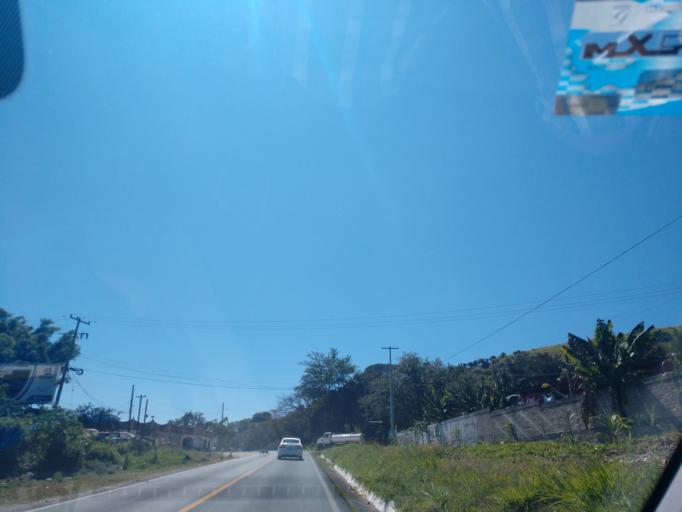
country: MX
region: Nayarit
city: Xalisco
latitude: 21.4099
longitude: -104.8970
